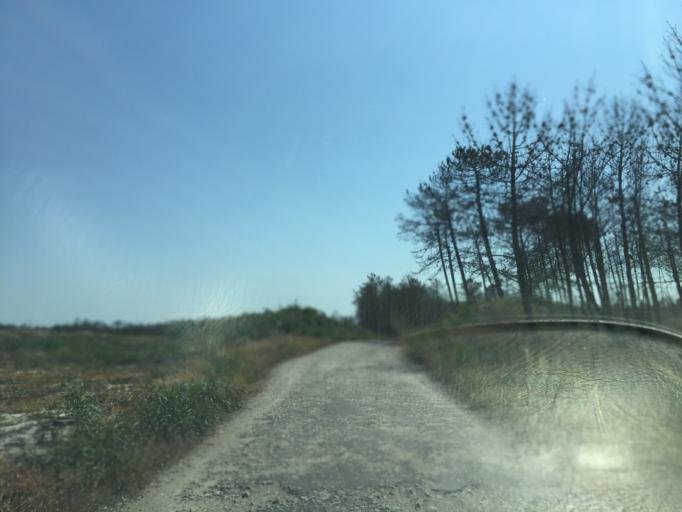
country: PT
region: Coimbra
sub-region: Figueira da Foz
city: Alhadas
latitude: 40.2586
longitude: -8.8354
